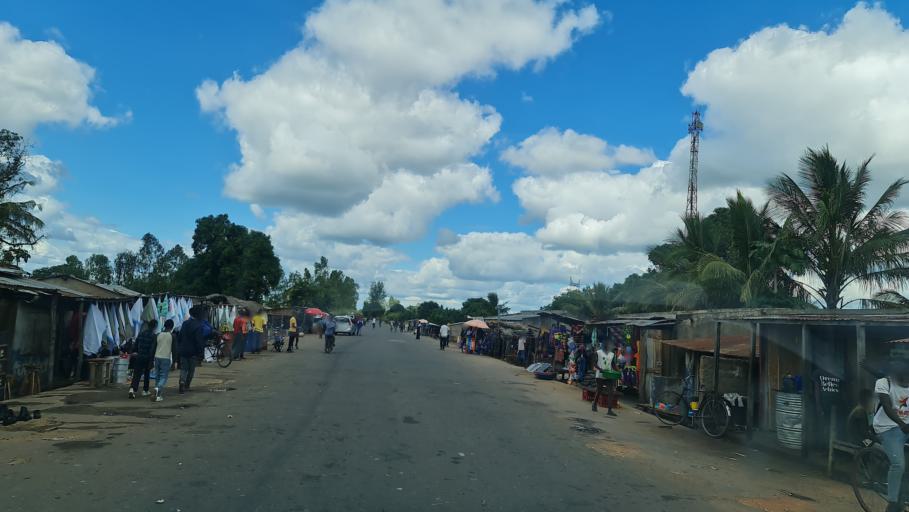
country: MZ
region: Zambezia
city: Quelimane
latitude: -17.5217
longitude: 36.2657
